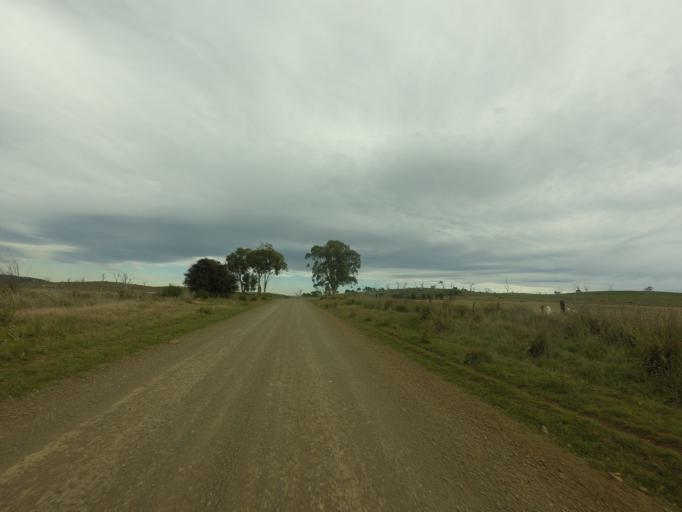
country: AU
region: Tasmania
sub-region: Derwent Valley
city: New Norfolk
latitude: -42.3950
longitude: 146.9723
